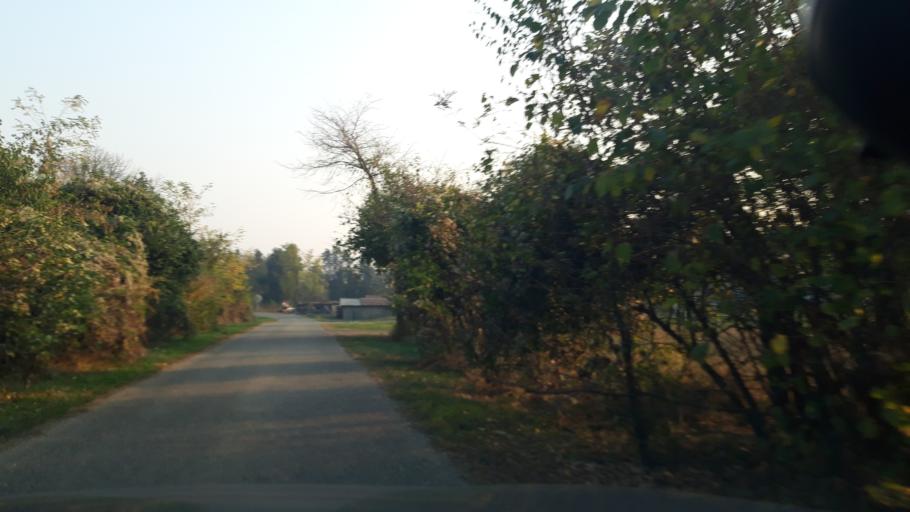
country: RS
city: Cortanovci
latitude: 45.1309
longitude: 19.9885
